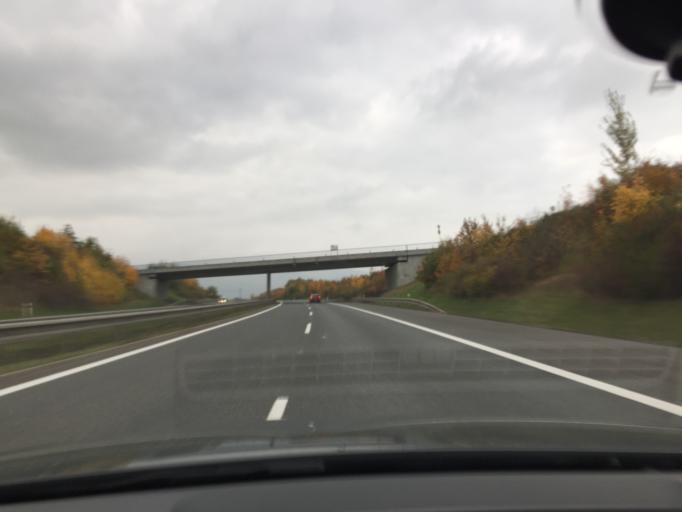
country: CZ
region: Ustecky
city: Trmice
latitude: 50.6660
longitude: 13.9776
